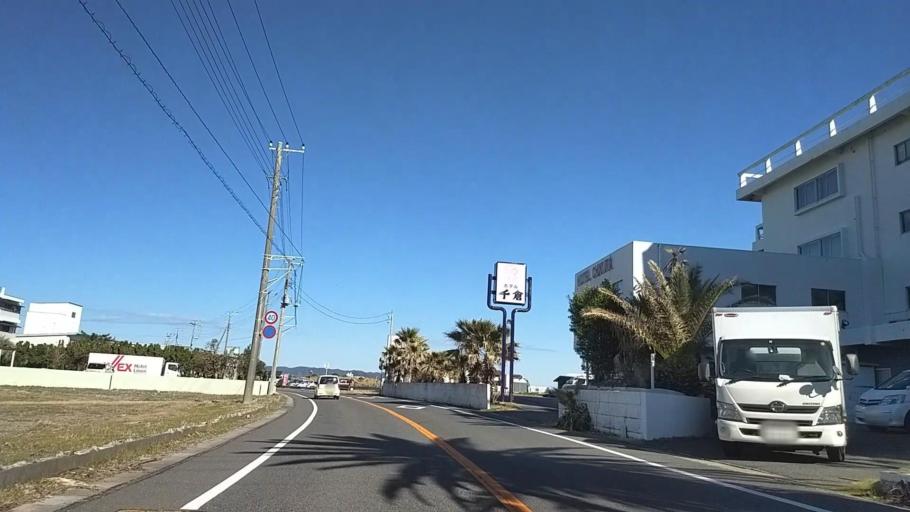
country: JP
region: Chiba
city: Tateyama
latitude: 34.9784
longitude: 139.9662
